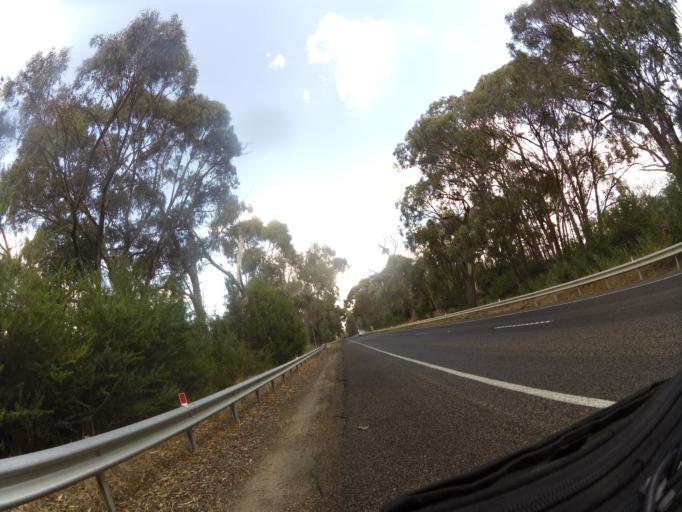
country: AU
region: Victoria
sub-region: Mansfield
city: Mansfield
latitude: -36.8322
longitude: 146.0082
